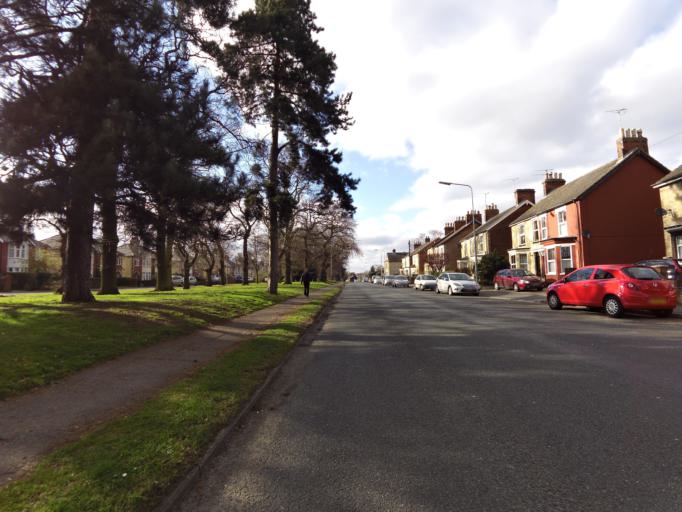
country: GB
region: England
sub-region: Suffolk
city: Ipswich
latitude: 52.0458
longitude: 1.1789
